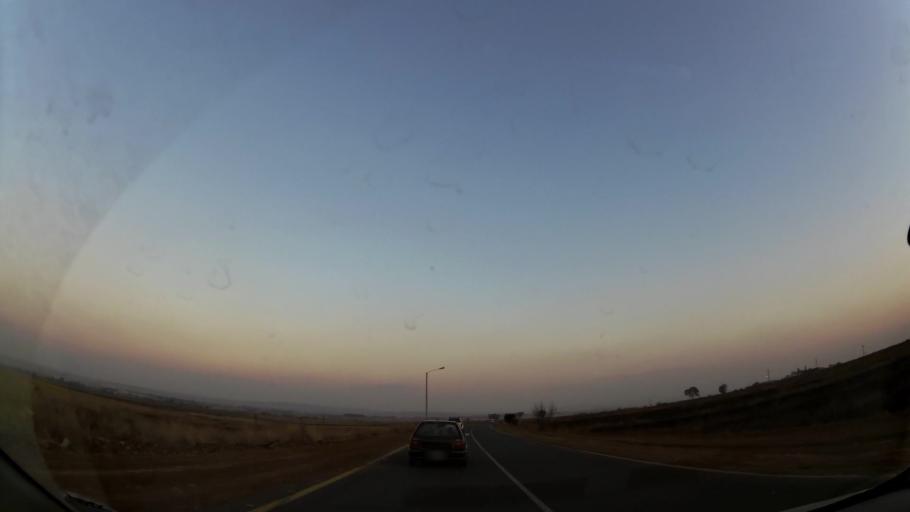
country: ZA
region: Gauteng
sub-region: Ekurhuleni Metropolitan Municipality
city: Nigel
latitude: -26.3685
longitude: 28.4207
